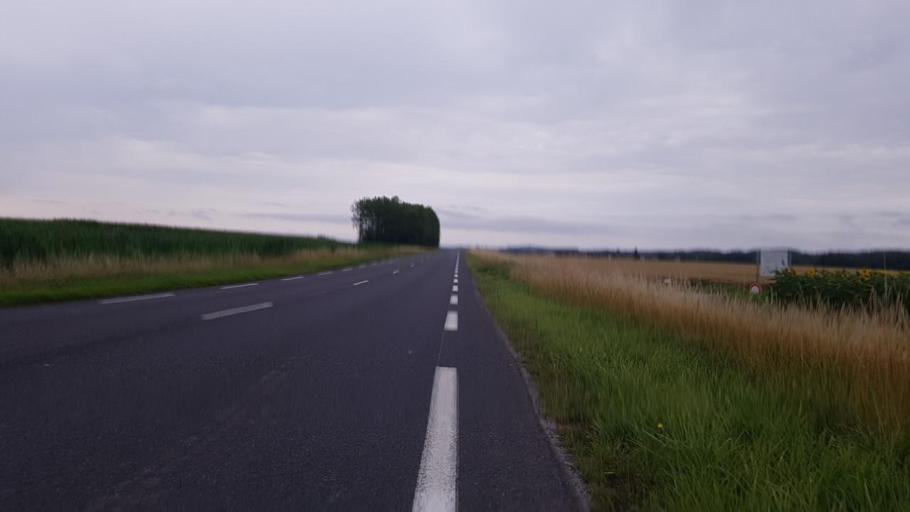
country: FR
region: Champagne-Ardenne
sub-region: Departement de la Marne
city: Pargny-sur-Saulx
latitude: 48.7605
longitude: 4.7725
